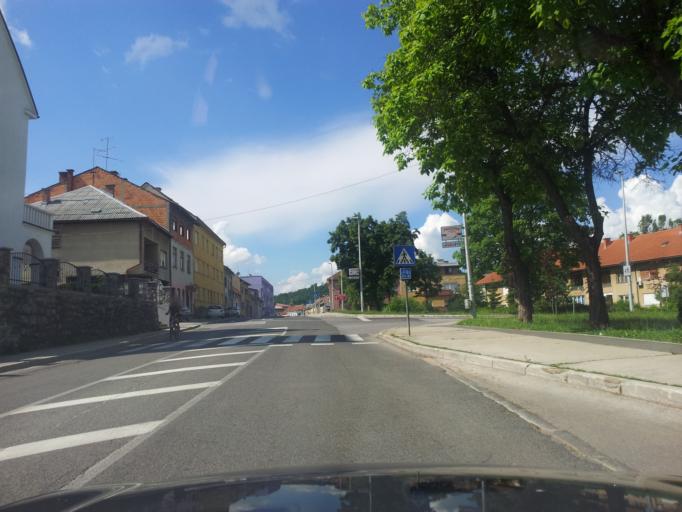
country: HR
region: Karlovacka
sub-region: Grad Karlovac
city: Karlovac
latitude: 45.4449
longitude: 15.5029
